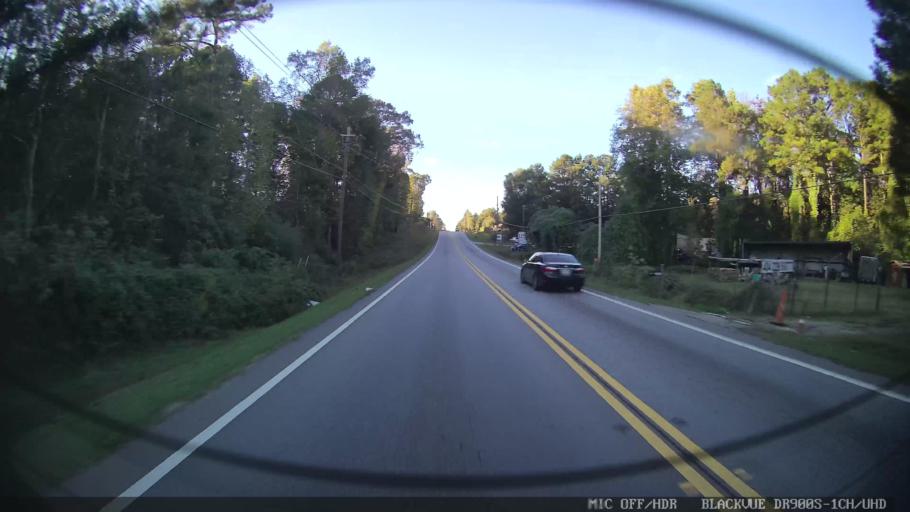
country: US
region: Georgia
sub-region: Clayton County
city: Lake City
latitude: 33.5988
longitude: -84.2977
